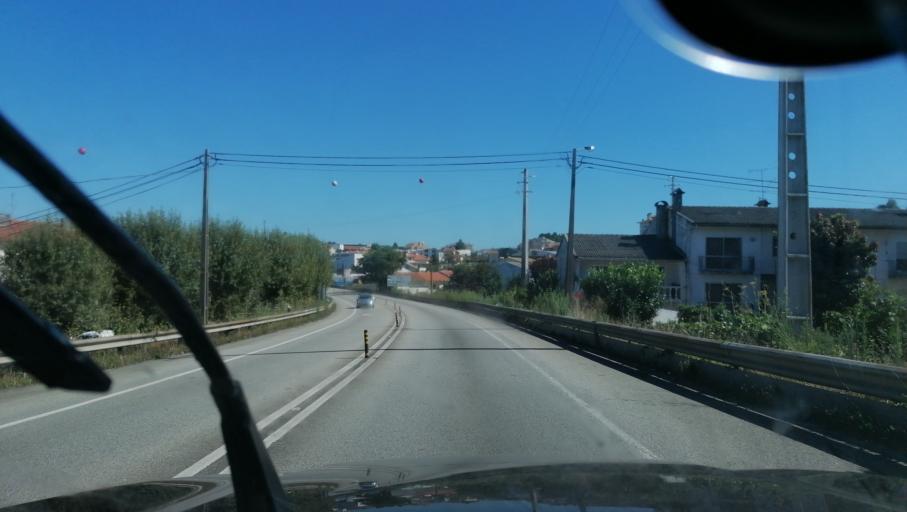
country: PT
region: Aveiro
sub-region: Santa Maria da Feira
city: Arrifana
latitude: 40.9221
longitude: -8.5014
